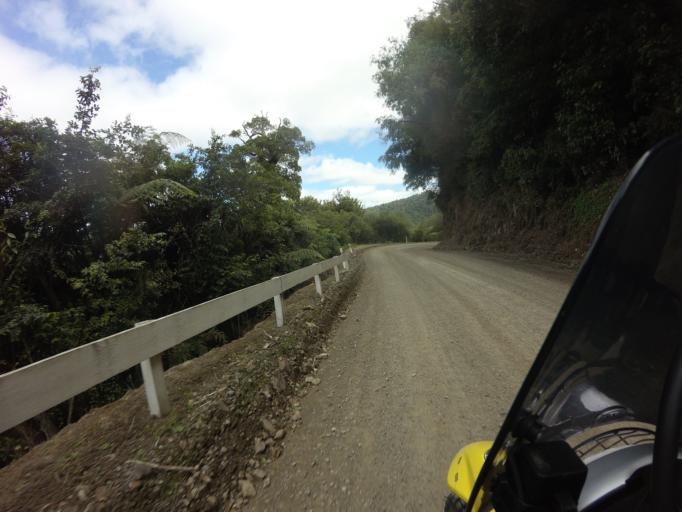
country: NZ
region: Bay of Plenty
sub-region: Whakatane District
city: Murupara
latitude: -38.6200
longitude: 177.0011
